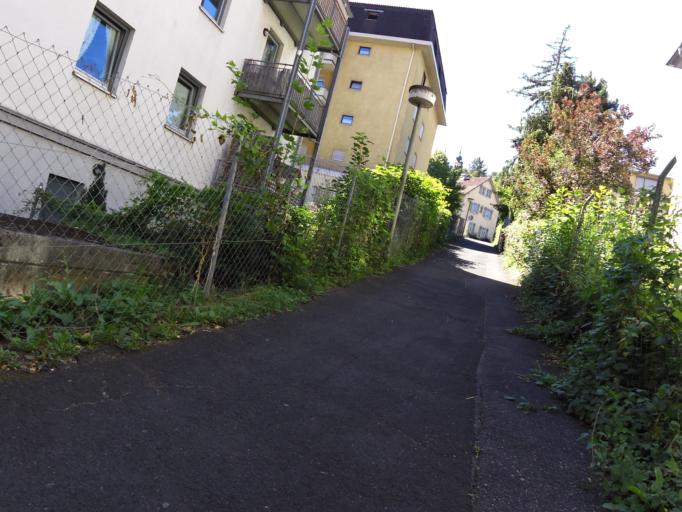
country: DE
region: Bavaria
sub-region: Regierungsbezirk Unterfranken
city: Wuerzburg
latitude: 49.7876
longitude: 9.9217
